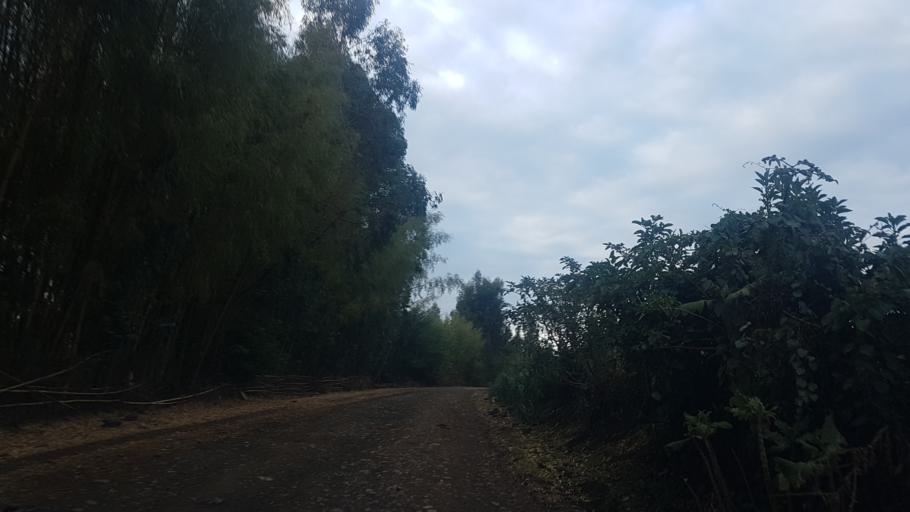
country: ET
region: Amhara
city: Finote Selam
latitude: 10.8035
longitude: 37.6621
